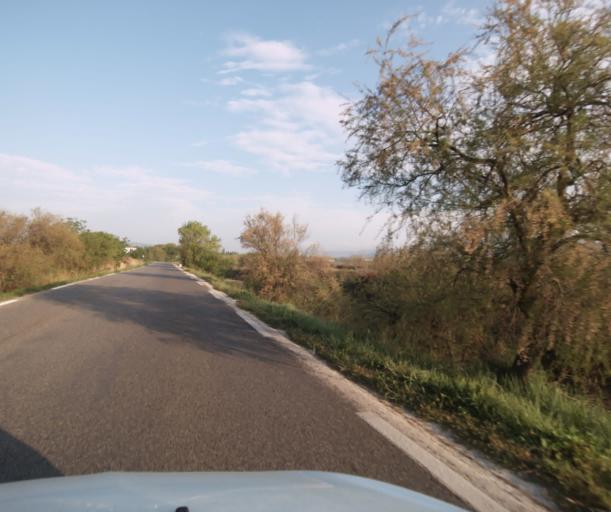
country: FR
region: Provence-Alpes-Cote d'Azur
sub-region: Departement du Var
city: La Londe-les-Maures
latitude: 43.1161
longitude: 6.1901
